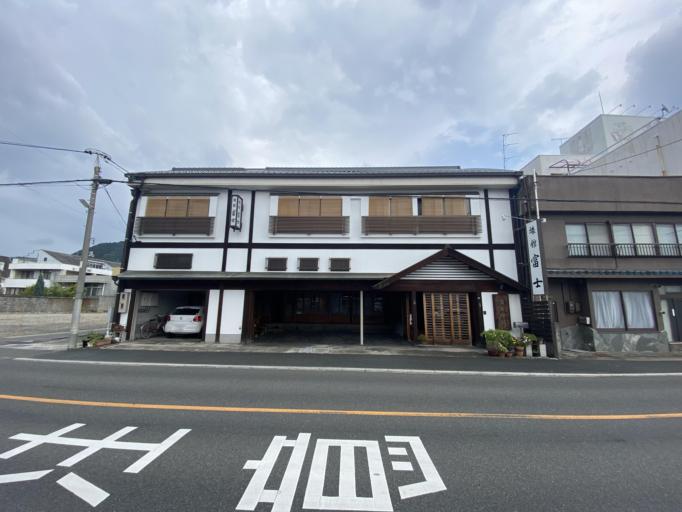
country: JP
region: Hiroshima
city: Fuchucho
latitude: 34.5724
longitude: 133.2350
